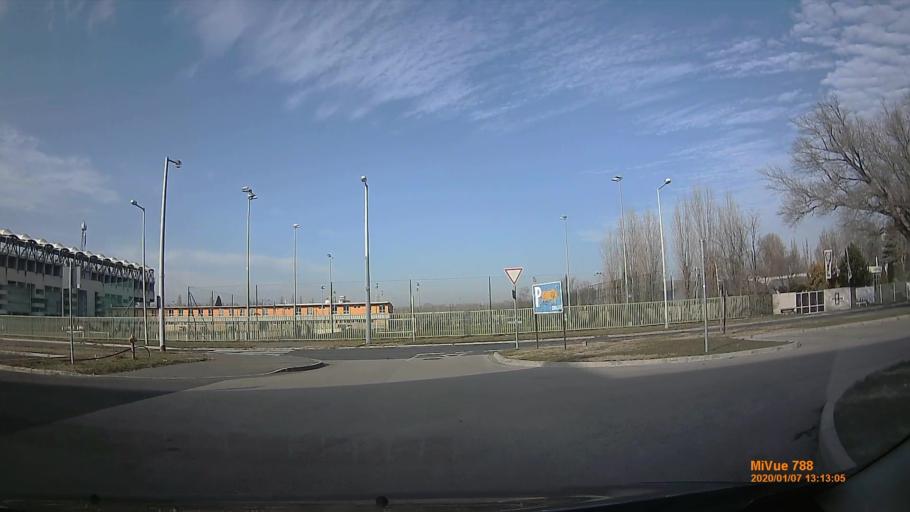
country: HU
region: Gyor-Moson-Sopron
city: Gyor
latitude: 47.6950
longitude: 17.6675
